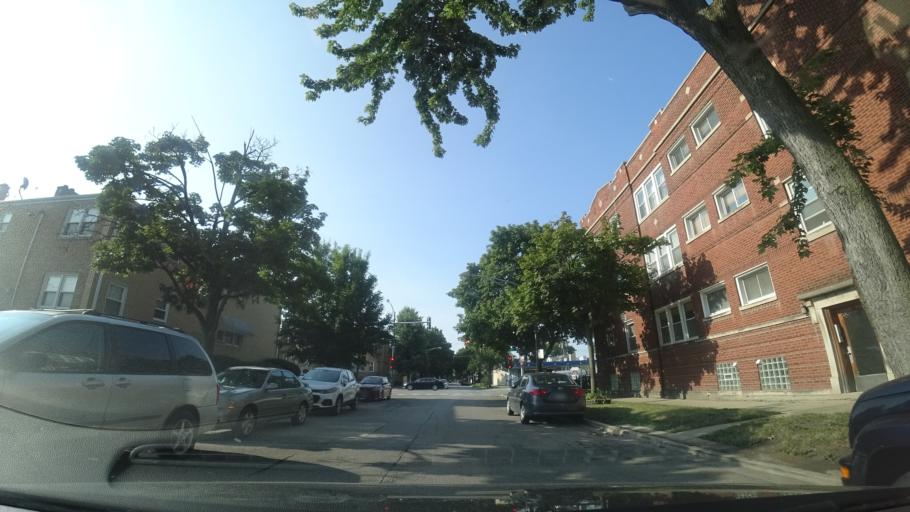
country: US
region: Illinois
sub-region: Cook County
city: Harwood Heights
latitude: 41.9610
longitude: -87.7624
